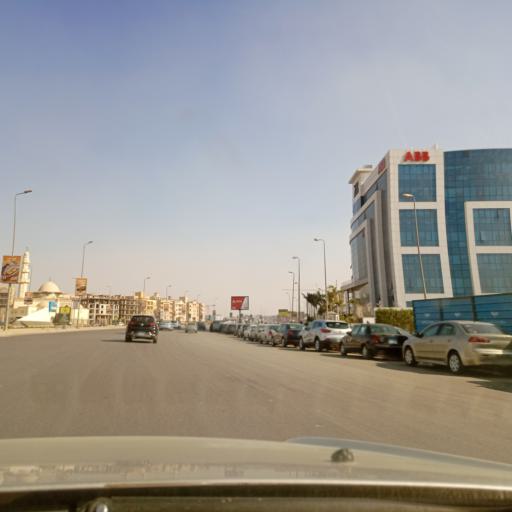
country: EG
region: Muhafazat al Qalyubiyah
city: Al Khankah
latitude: 30.0303
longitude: 31.4656
